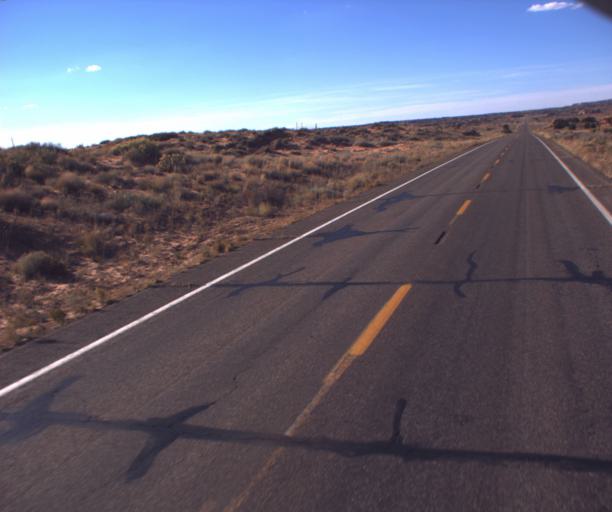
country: US
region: Arizona
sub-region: Coconino County
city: Kaibito
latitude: 36.6013
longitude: -111.1718
